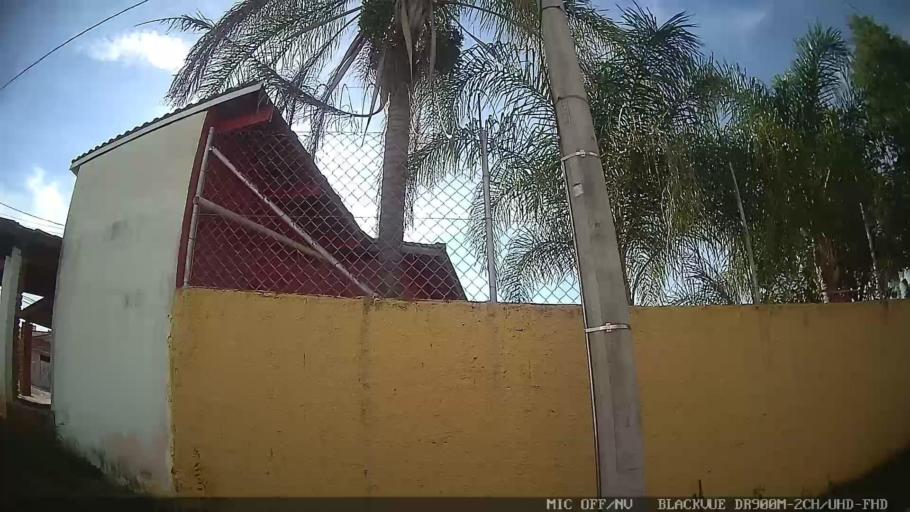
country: BR
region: Sao Paulo
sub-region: Tiete
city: Tiete
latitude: -23.0885
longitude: -47.6958
